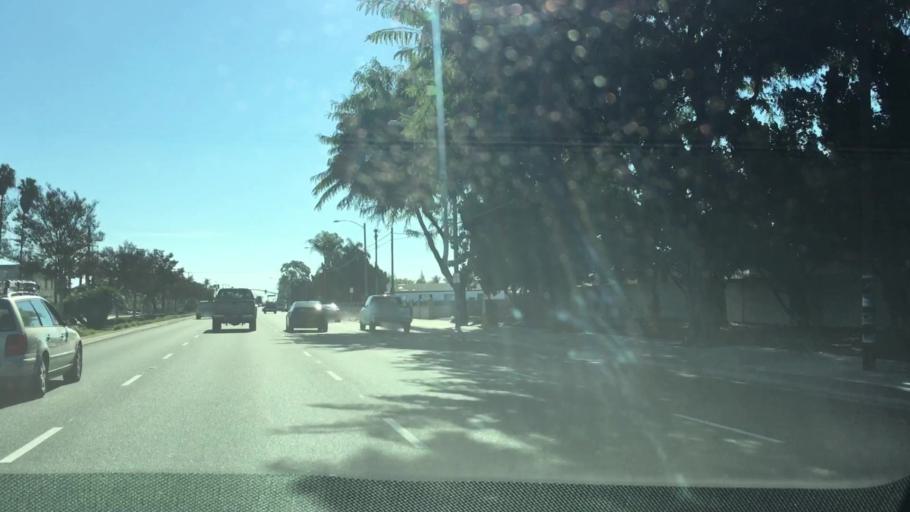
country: US
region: California
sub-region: Orange County
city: Stanton
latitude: 33.8308
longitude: -117.9936
